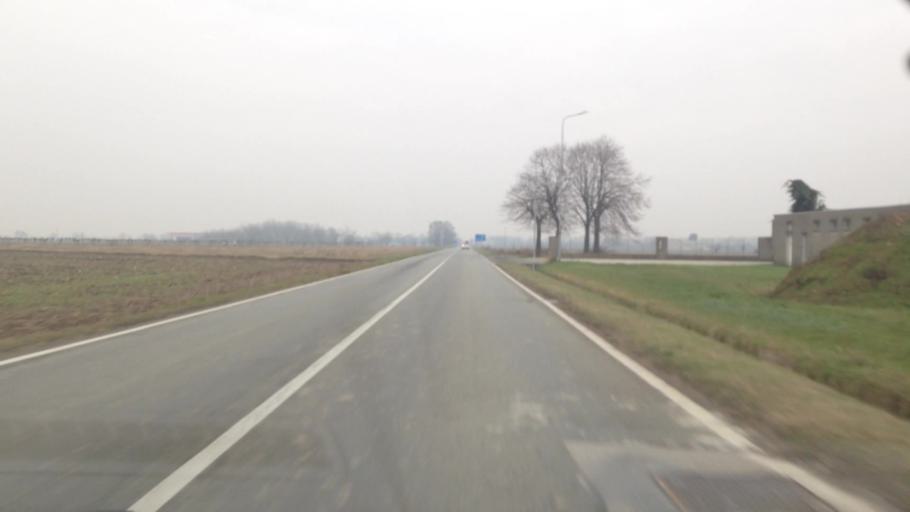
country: IT
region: Piedmont
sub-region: Provincia di Vercelli
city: Bianze
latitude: 45.3242
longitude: 8.0868
